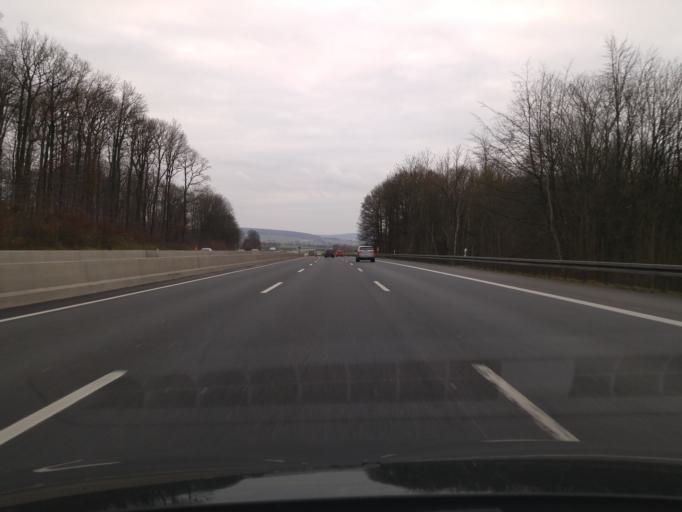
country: DE
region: Lower Saxony
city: Haverlah
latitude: 52.0350
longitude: 10.1742
